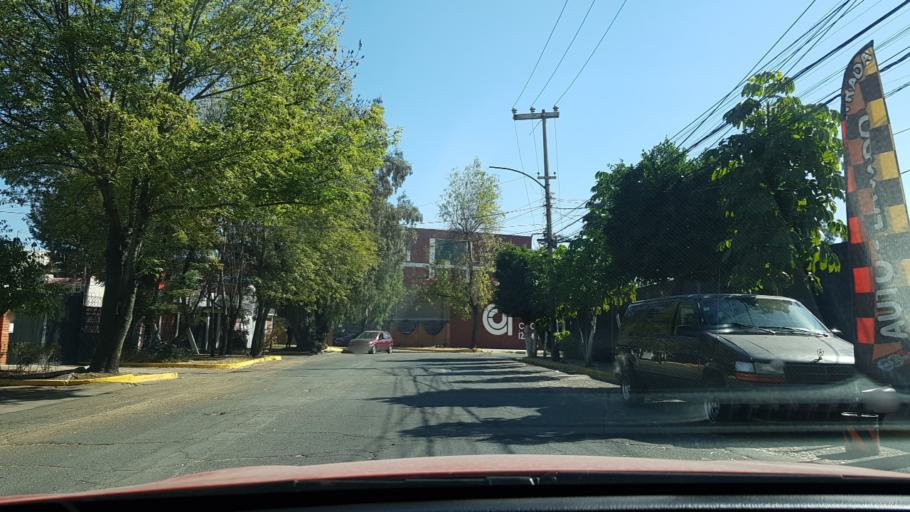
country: MX
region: Mexico
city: Cuautitlan Izcalli
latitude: 19.6518
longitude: -99.2039
